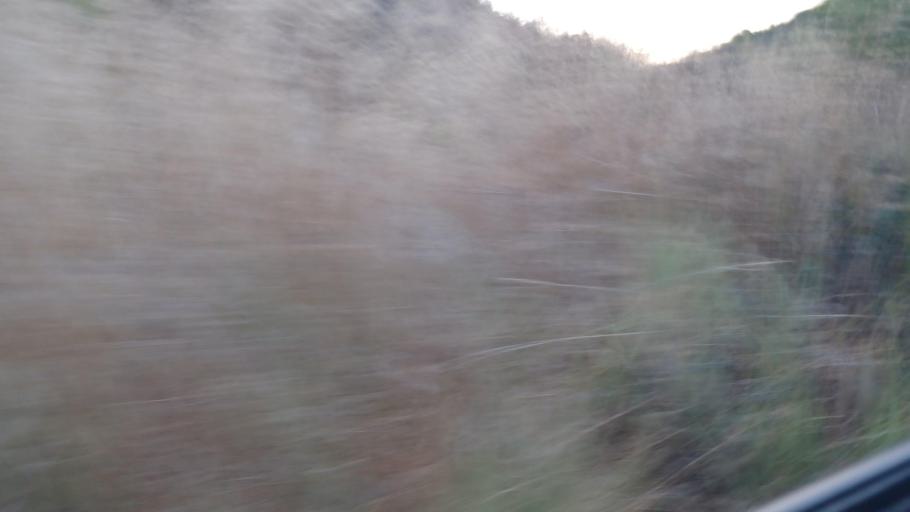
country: CY
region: Pafos
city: Mesogi
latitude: 34.8746
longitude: 32.5220
